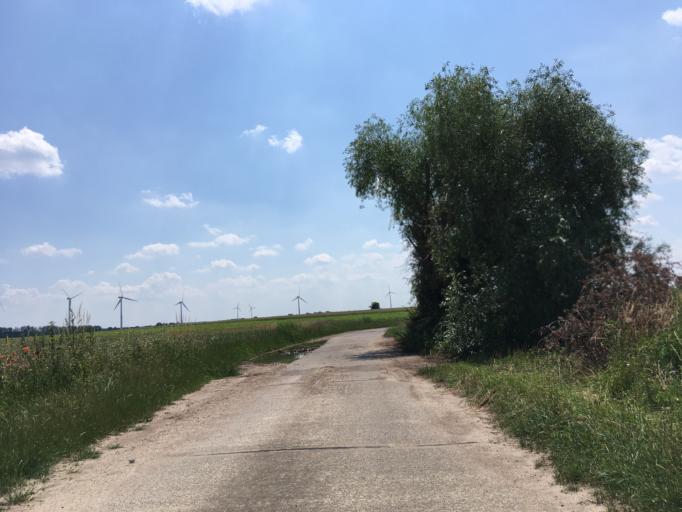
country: DE
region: Brandenburg
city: Werftpfuhl
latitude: 52.7131
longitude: 13.8277
